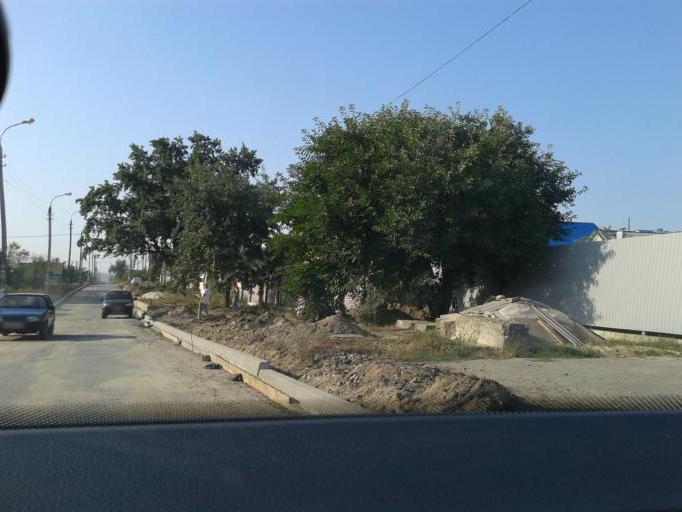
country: RU
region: Volgograd
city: Volgograd
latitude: 48.6145
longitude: 44.4140
